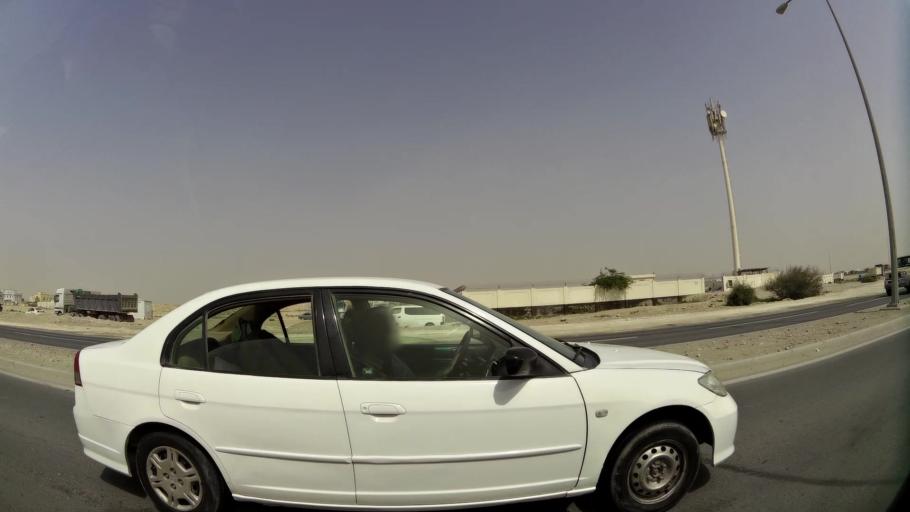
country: QA
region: Baladiyat ar Rayyan
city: Ar Rayyan
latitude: 25.2302
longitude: 51.3849
